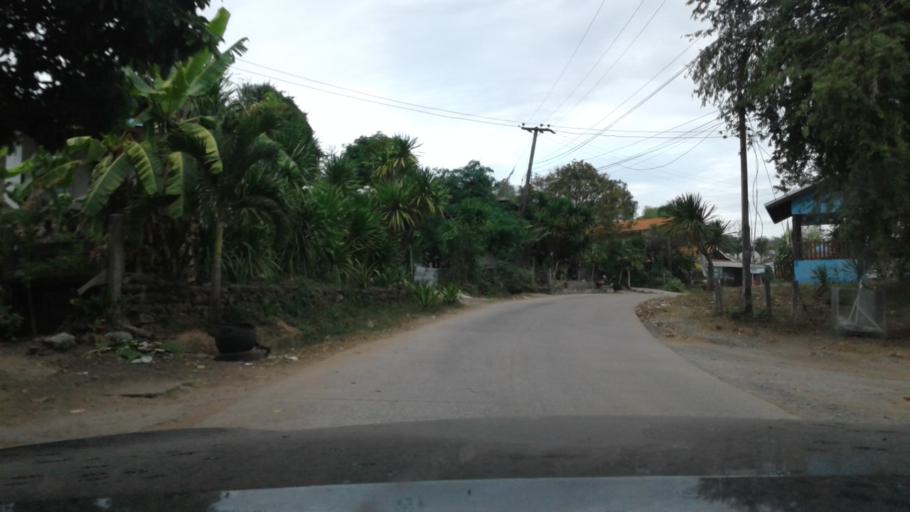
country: TH
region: Changwat Udon Thani
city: Nong Wua So
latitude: 17.2350
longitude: 102.5329
